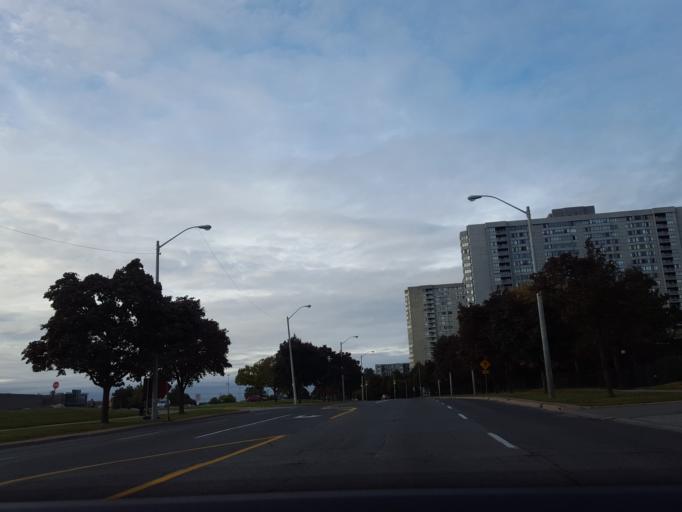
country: CA
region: Ontario
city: Scarborough
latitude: 43.7973
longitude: -79.3159
